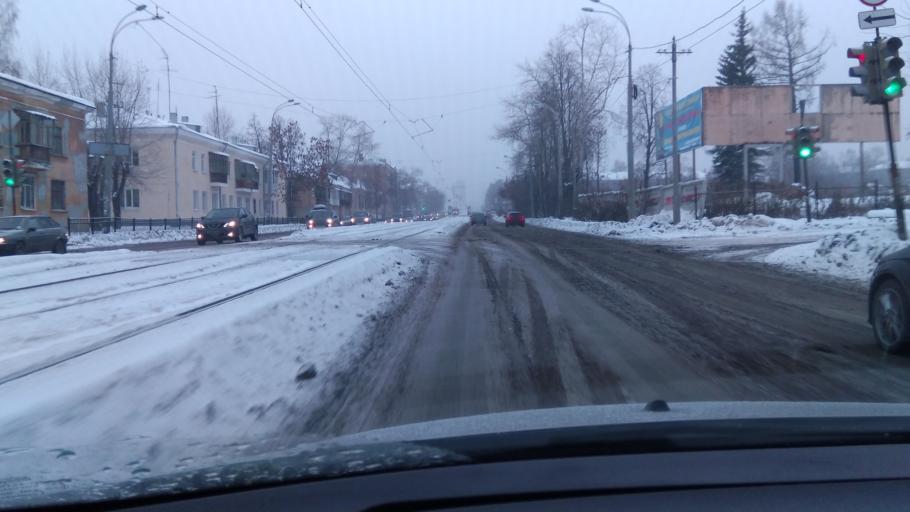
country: RU
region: Sverdlovsk
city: Yekaterinburg
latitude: 56.9001
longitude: 60.5811
